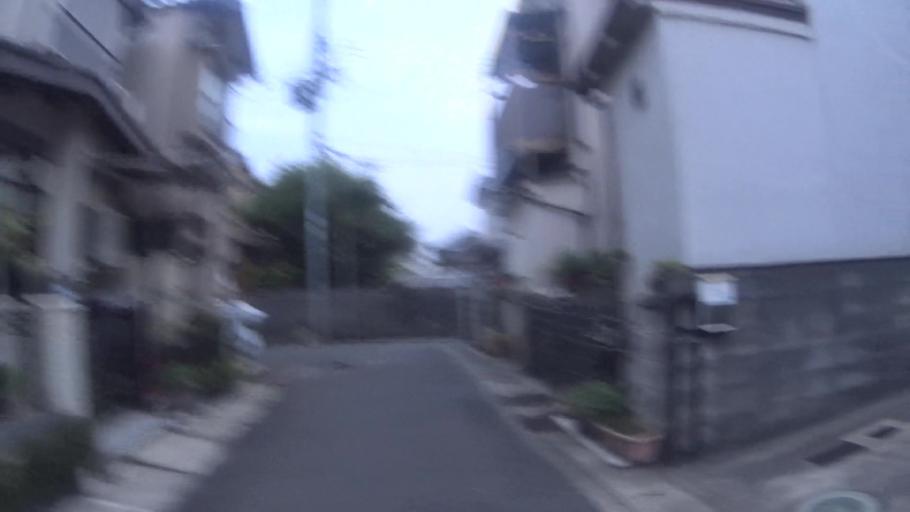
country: JP
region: Kyoto
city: Muko
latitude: 34.9448
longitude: 135.7076
